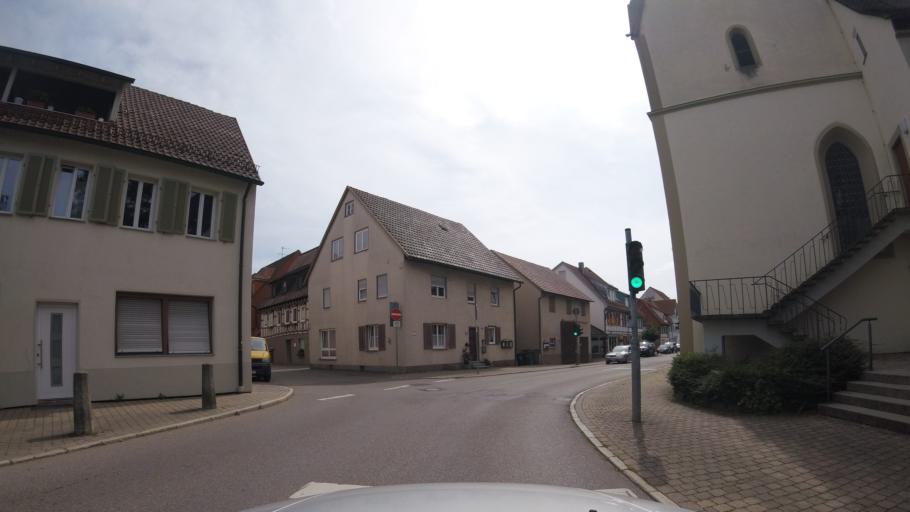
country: DE
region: Baden-Wuerttemberg
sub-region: Regierungsbezirk Stuttgart
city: Grossbottwar
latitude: 49.0013
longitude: 9.2916
